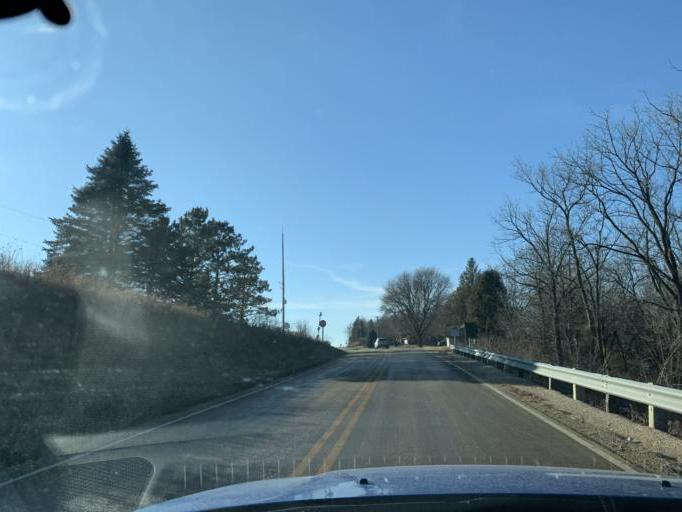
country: US
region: Wisconsin
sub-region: Iowa County
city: Barneveld
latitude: 42.8075
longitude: -89.8725
